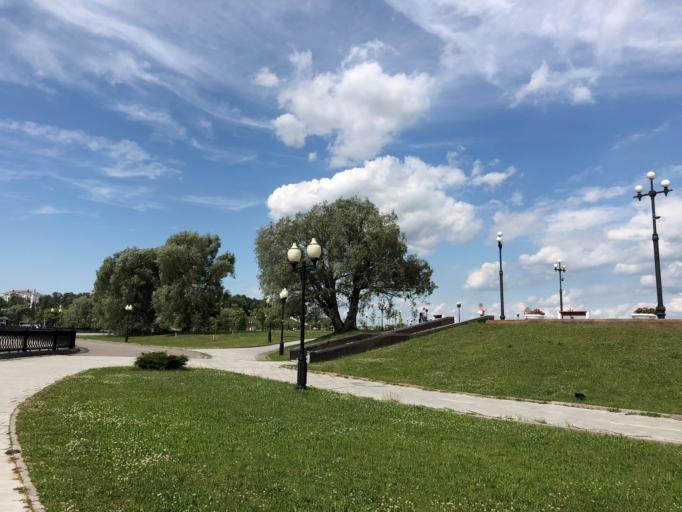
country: RU
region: Jaroslavl
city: Yaroslavl
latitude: 57.6172
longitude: 39.9042
